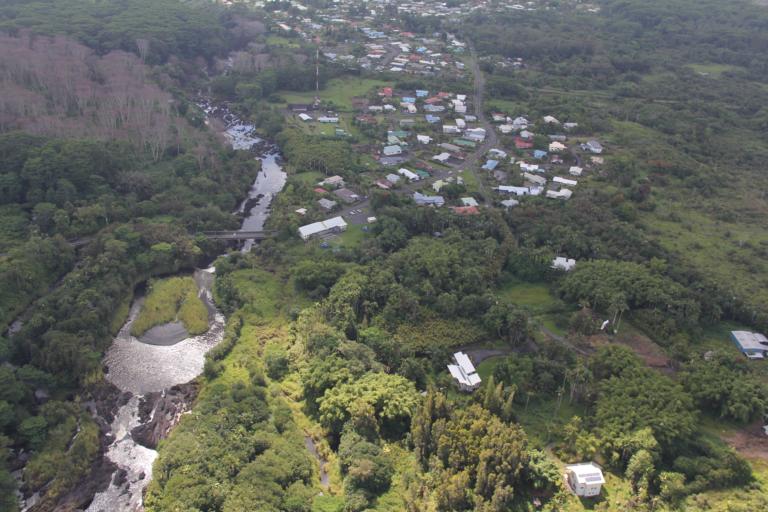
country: US
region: Hawaii
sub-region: Hawaii County
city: Hilo
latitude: 19.7173
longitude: -155.1398
